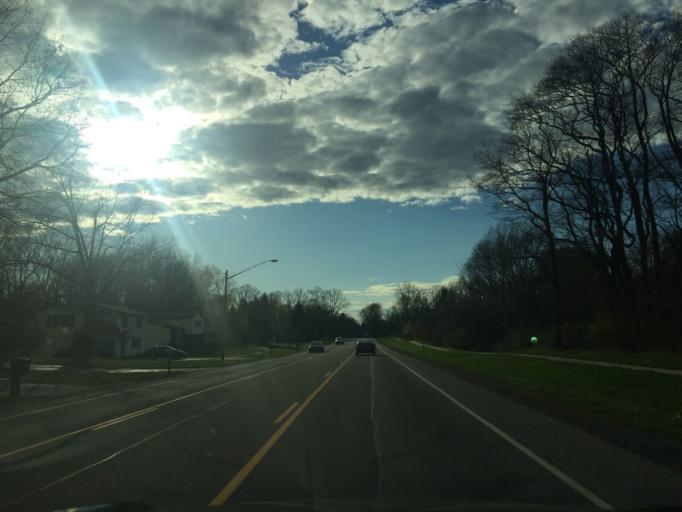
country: US
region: New York
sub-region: Monroe County
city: Irondequoit
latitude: 43.2445
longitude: -77.5851
